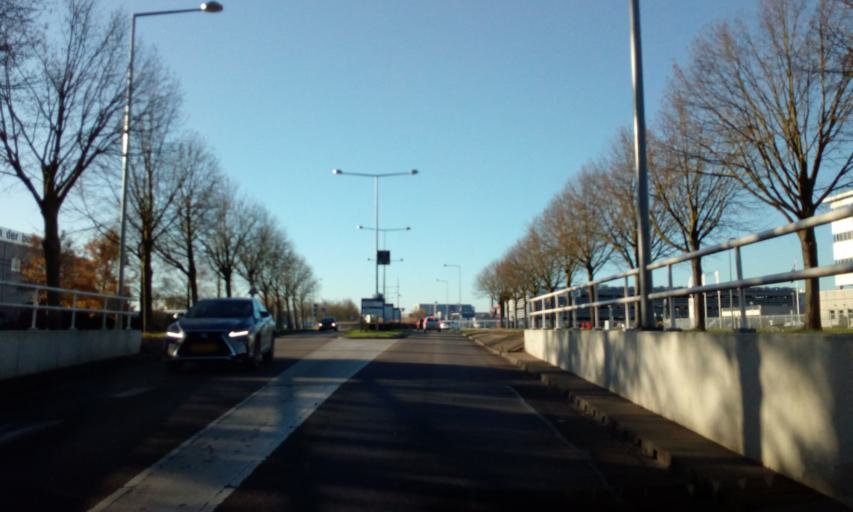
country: NL
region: South Holland
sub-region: Gemeente Leidschendam-Voorburg
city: Voorburg
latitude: 52.0695
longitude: 4.3916
